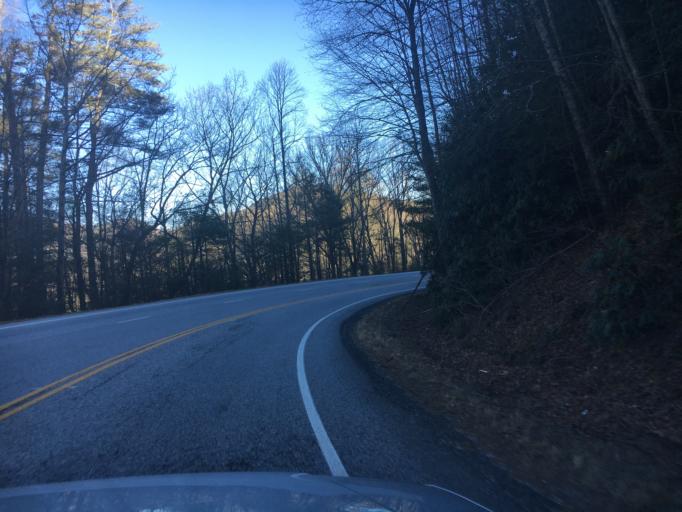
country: US
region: Georgia
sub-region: White County
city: Cleveland
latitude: 34.6861
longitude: -83.8981
